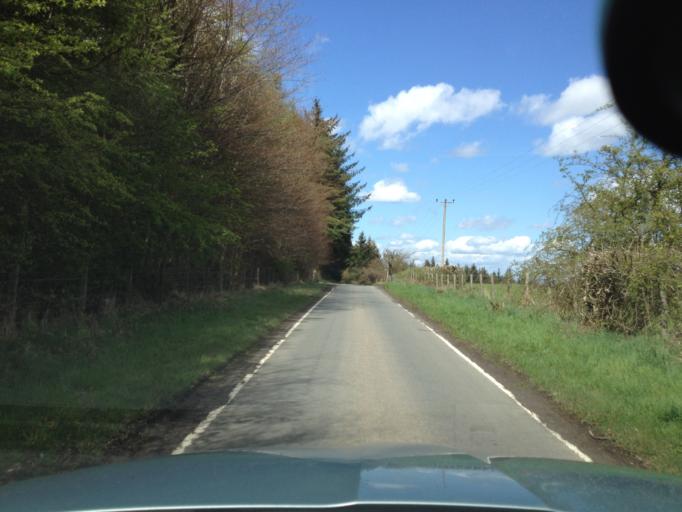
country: GB
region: Scotland
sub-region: West Lothian
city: Linlithgow
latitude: 55.9453
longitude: -3.5883
